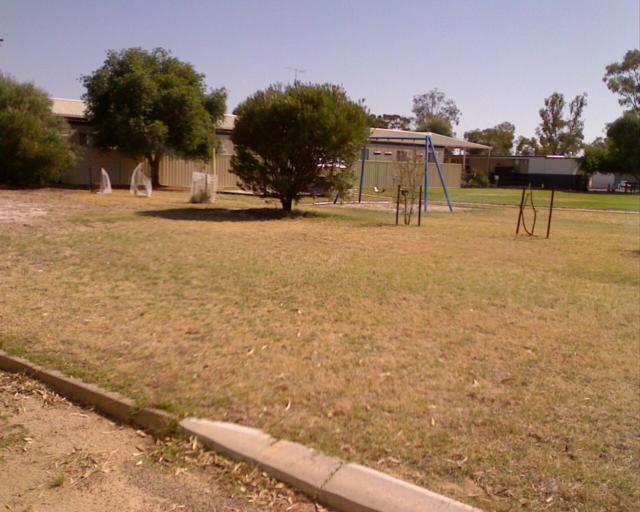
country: AU
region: Western Australia
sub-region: Cunderdin
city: Cunderdin
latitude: -31.6246
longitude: 117.7167
